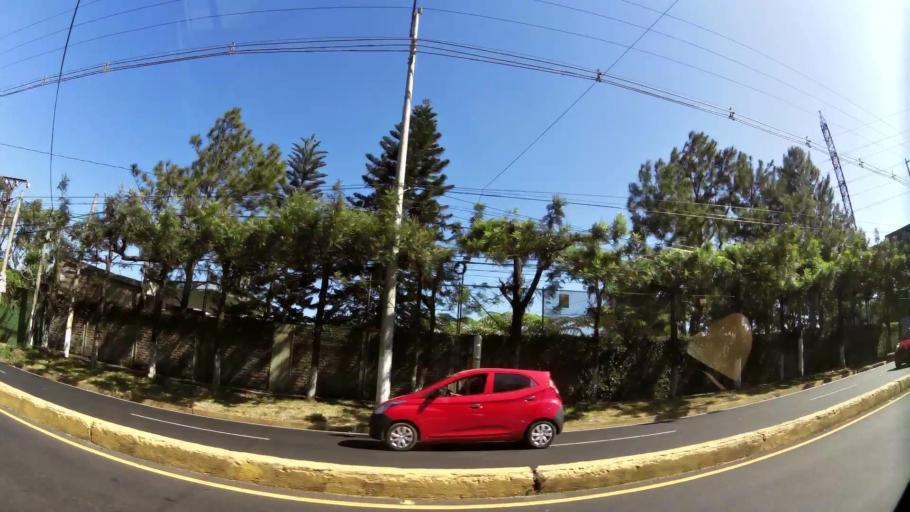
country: SV
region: La Libertad
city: Santa Tecla
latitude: 13.6637
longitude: -89.2787
